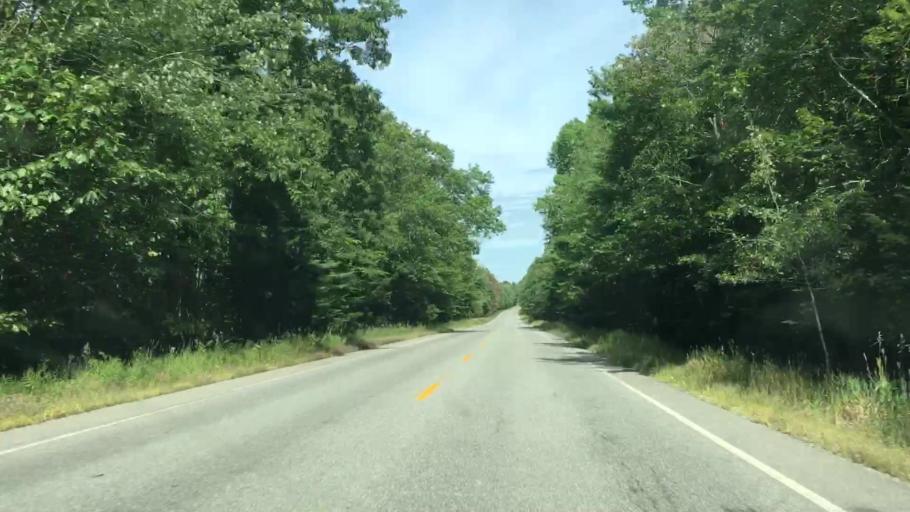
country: US
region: Maine
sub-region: Penobscot County
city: Lincoln
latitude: 45.3841
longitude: -68.5417
